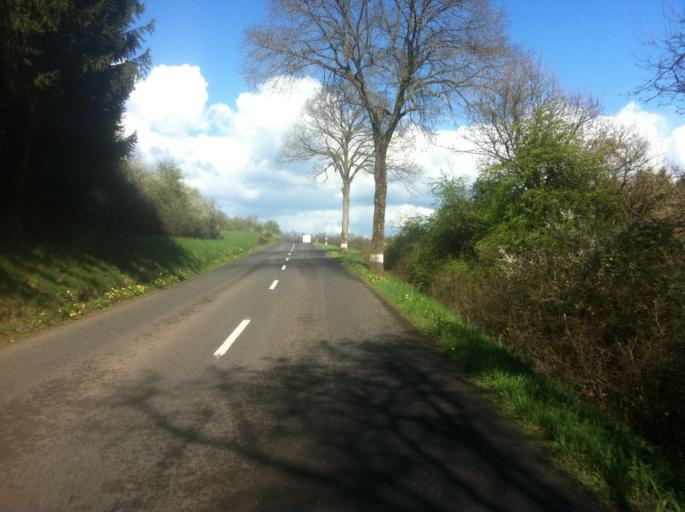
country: LU
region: Diekirch
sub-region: Canton de Clervaux
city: Clervaux
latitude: 50.0218
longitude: 6.0281
